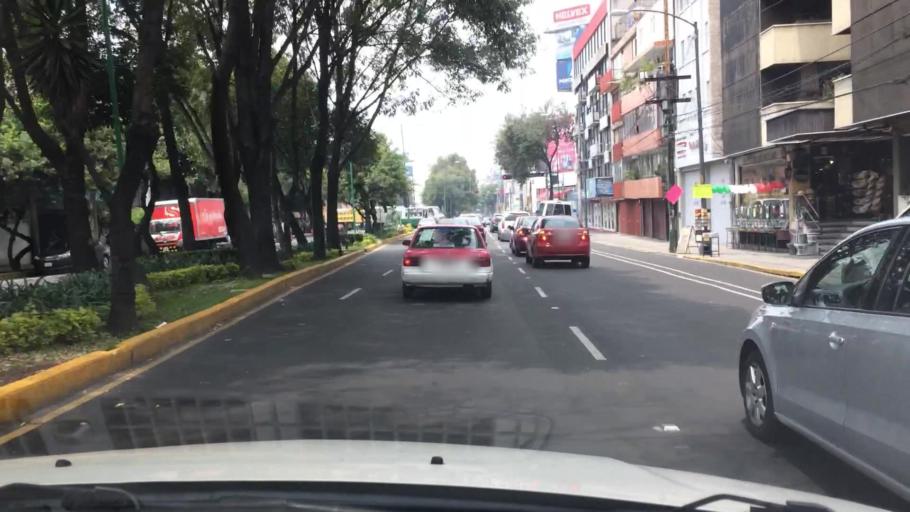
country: MX
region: Mexico City
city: Coyoacan
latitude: 19.3608
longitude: -99.1539
